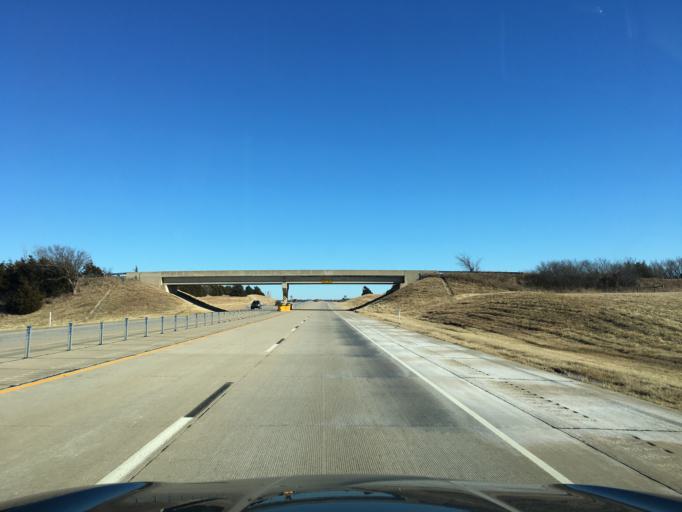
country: US
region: Oklahoma
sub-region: Payne County
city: Yale
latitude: 36.2251
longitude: -96.6258
